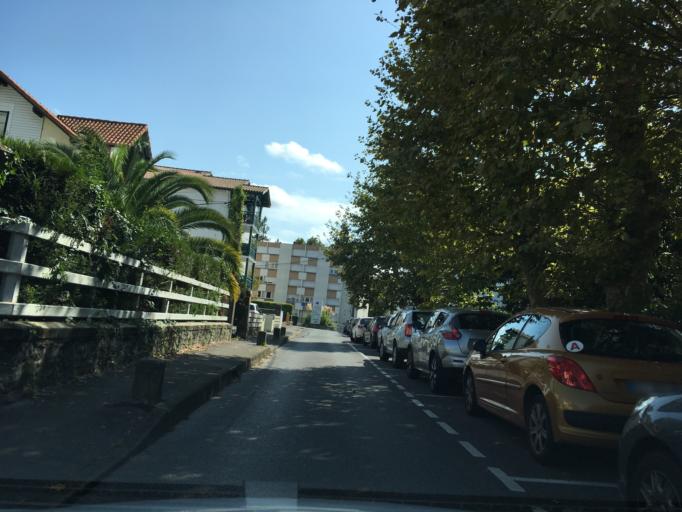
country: FR
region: Aquitaine
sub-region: Departement des Pyrenees-Atlantiques
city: Bayonne
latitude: 43.4861
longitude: -1.4877
